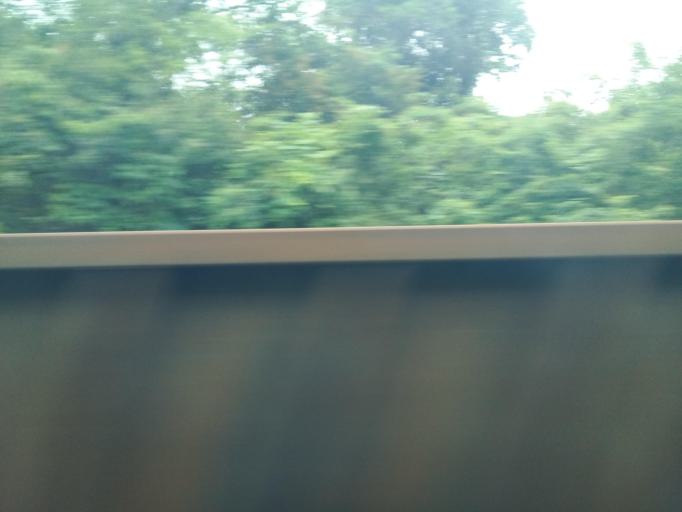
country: BR
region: Minas Gerais
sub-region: Rio Piracicaba
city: Rio Piracicaba
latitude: -19.9682
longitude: -43.2529
